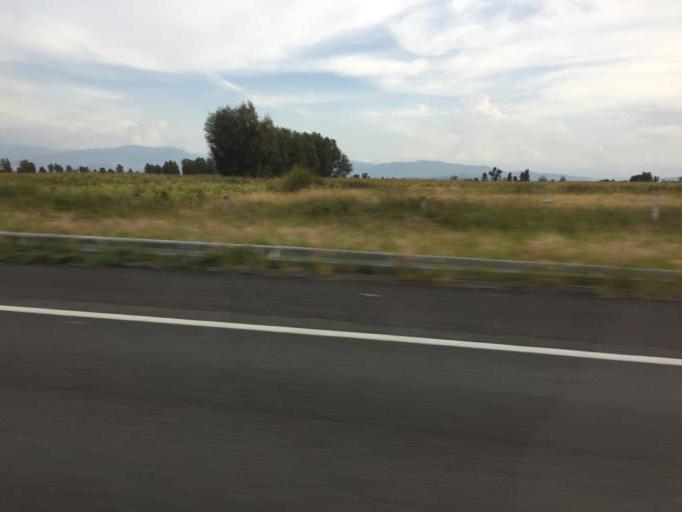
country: MX
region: Michoacan
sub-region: Alvaro Obregon
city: Tzintzimeo
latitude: 19.8913
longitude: -100.9955
